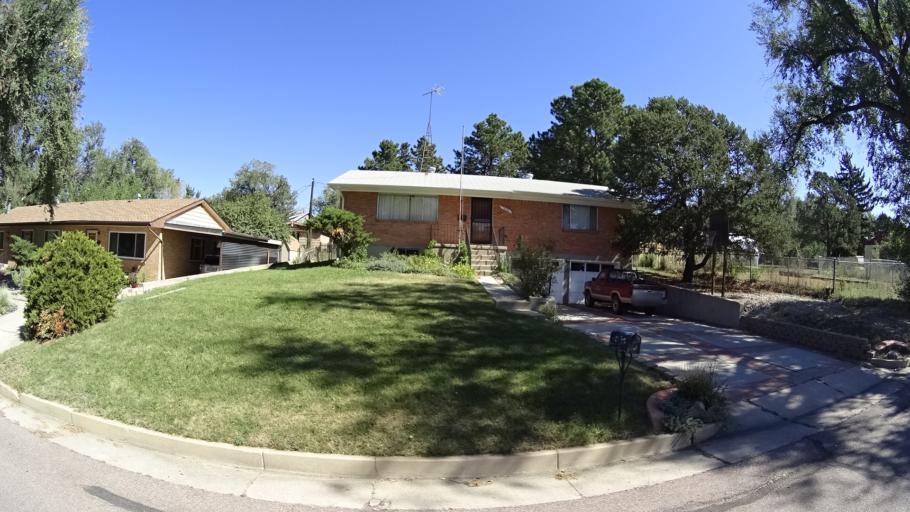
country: US
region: Colorado
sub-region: El Paso County
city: Colorado Springs
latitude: 38.8453
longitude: -104.8457
